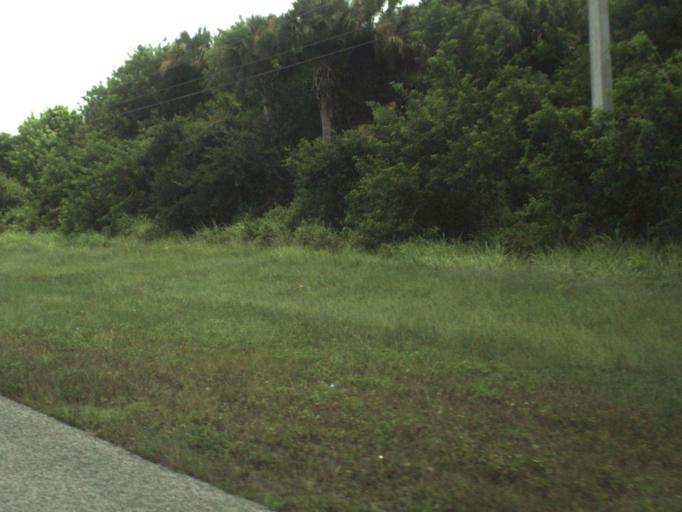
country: US
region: Florida
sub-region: Saint Lucie County
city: Fort Pierce South
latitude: 27.4007
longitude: -80.4516
